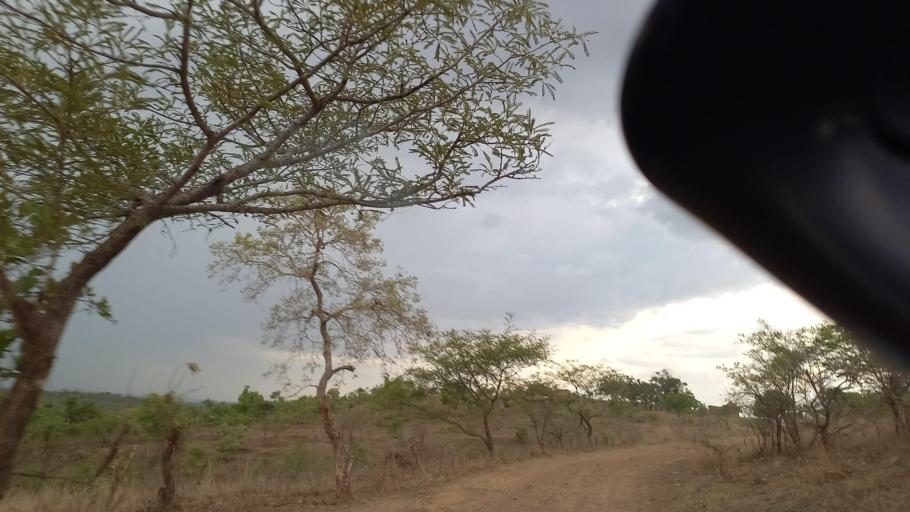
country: ZM
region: Lusaka
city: Kafue
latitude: -16.1232
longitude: 28.0613
